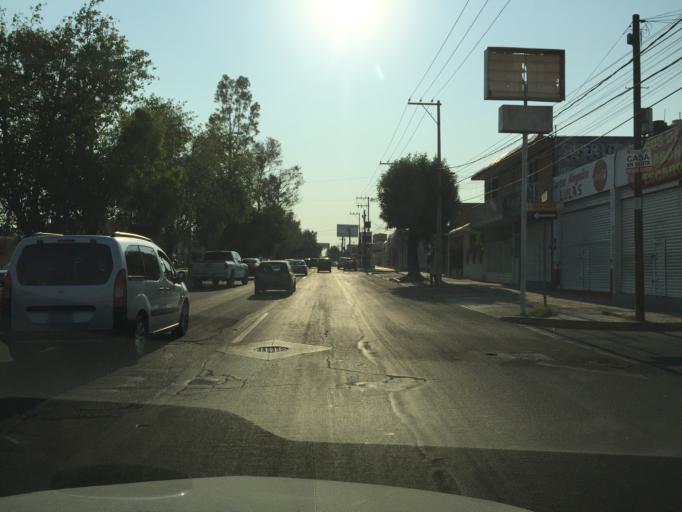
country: MX
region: Aguascalientes
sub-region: Aguascalientes
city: Aguascalientes
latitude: 21.8588
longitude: -102.3048
